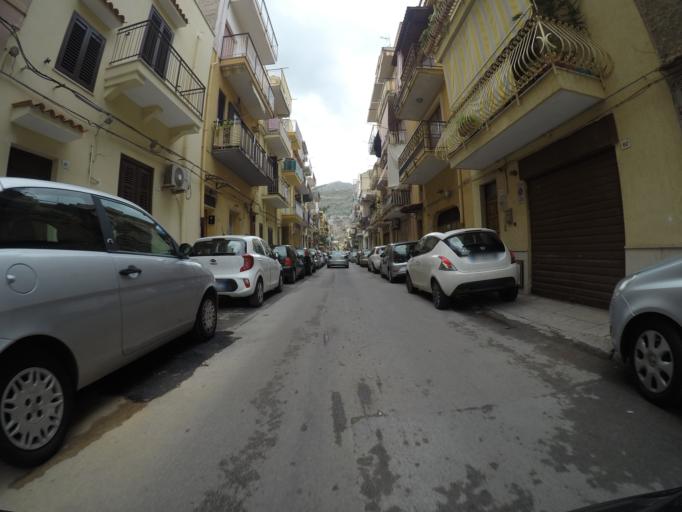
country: IT
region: Sicily
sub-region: Palermo
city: Isola delle Femmine
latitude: 38.2000
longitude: 13.2785
